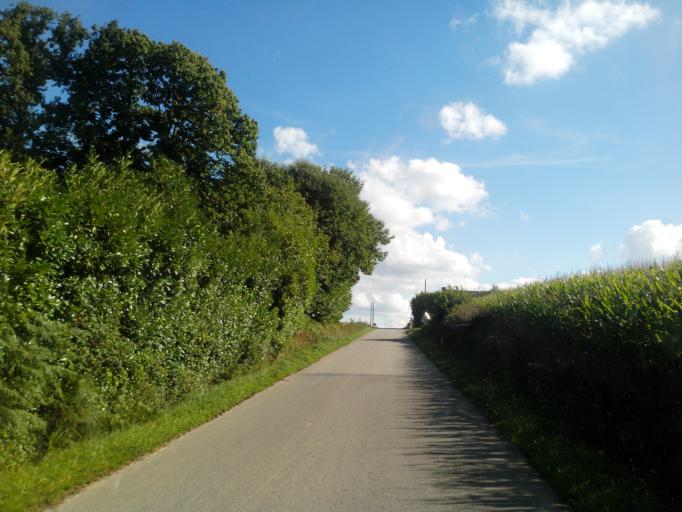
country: FR
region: Brittany
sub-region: Departement des Cotes-d'Armor
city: Merdrignac
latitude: 48.1434
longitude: -2.4021
